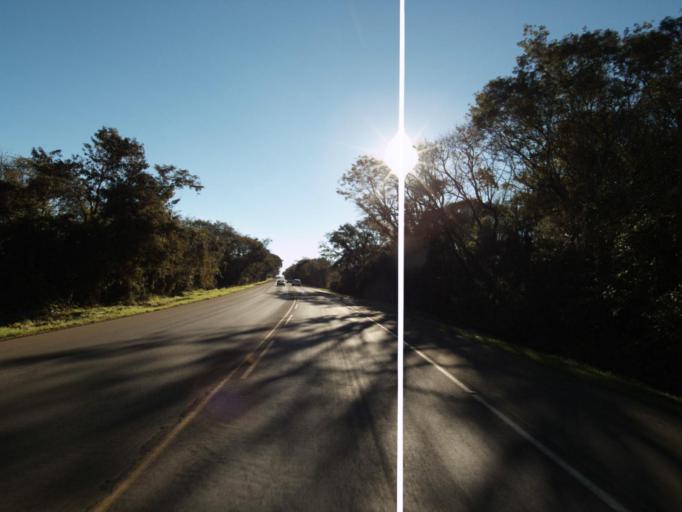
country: BR
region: Santa Catarina
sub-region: Chapeco
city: Chapeco
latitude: -26.9914
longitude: -52.7259
